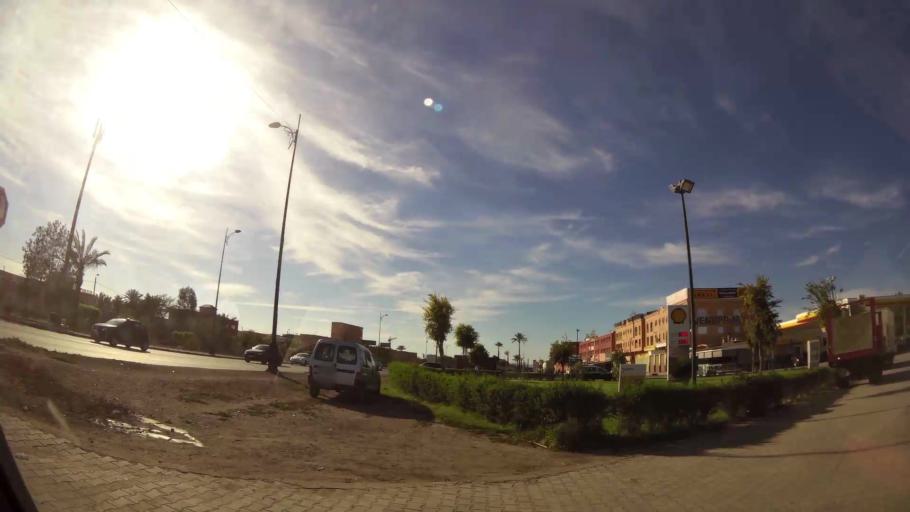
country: MA
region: Marrakech-Tensift-Al Haouz
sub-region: Marrakech
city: Marrakesh
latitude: 31.6701
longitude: -8.0367
